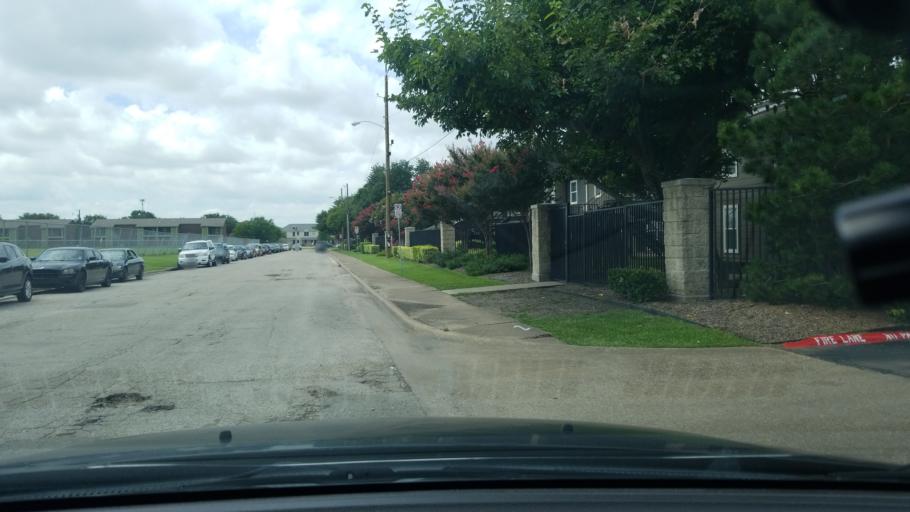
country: US
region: Texas
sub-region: Dallas County
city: Mesquite
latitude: 32.8126
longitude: -96.6685
